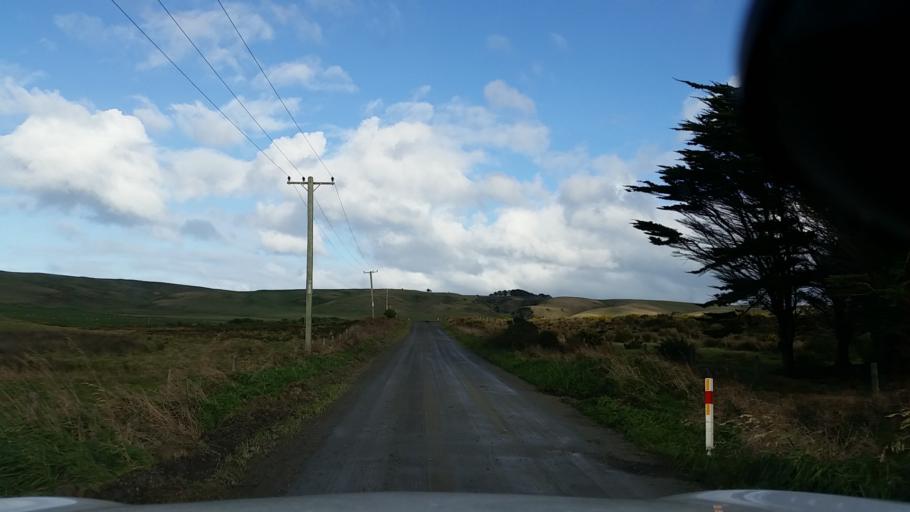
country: NZ
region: Chatham Islands
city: Waitangi
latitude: -44.0316
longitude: -176.3510
